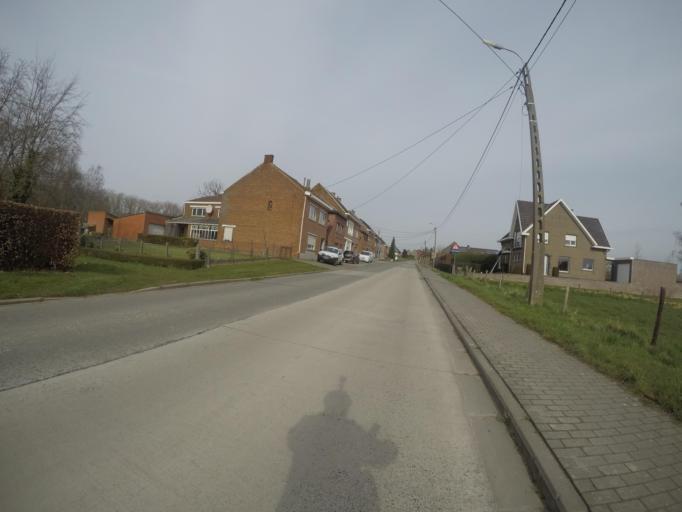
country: BE
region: Flanders
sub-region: Provincie Oost-Vlaanderen
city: Sint-Maria-Lierde
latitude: 50.8076
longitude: 3.8232
